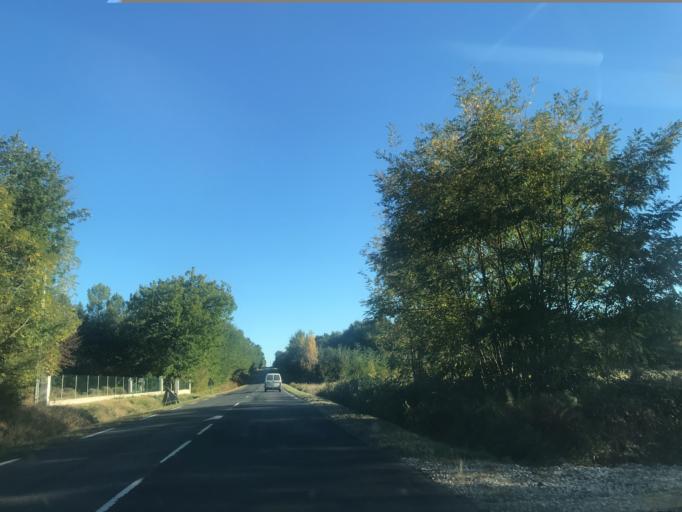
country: FR
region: Poitou-Charentes
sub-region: Departement de la Charente-Maritime
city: Montguyon
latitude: 45.1988
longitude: -0.1451
